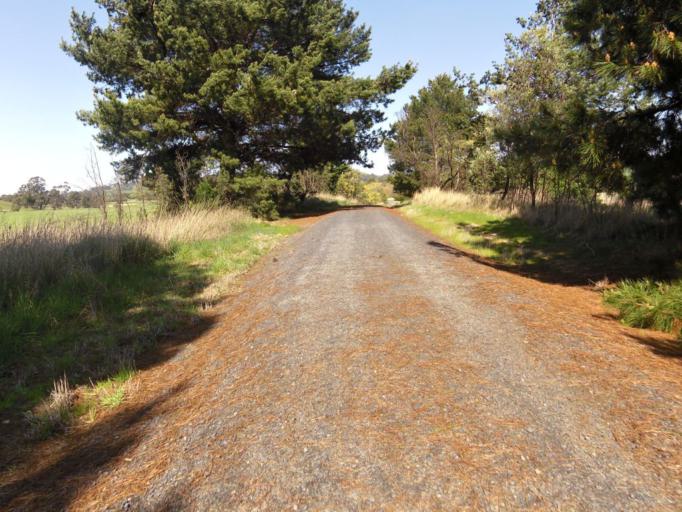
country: AU
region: Victoria
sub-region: Murrindindi
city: Alexandra
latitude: -37.0097
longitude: 145.7540
